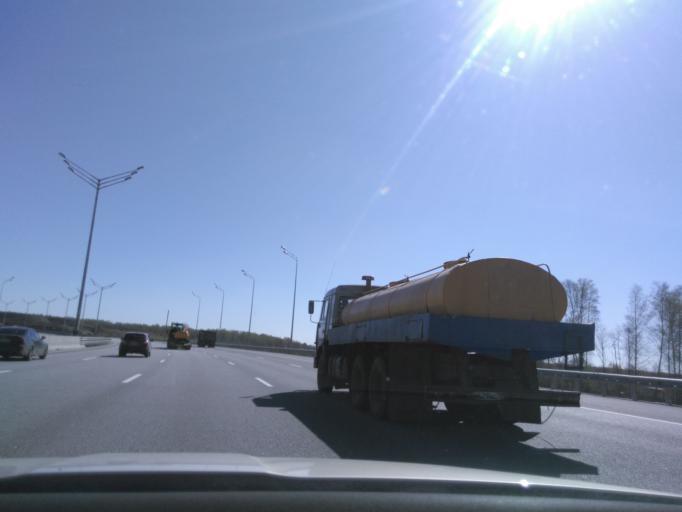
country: RU
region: Moskovskaya
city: Novopodrezkovo
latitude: 55.9537
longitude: 37.3797
